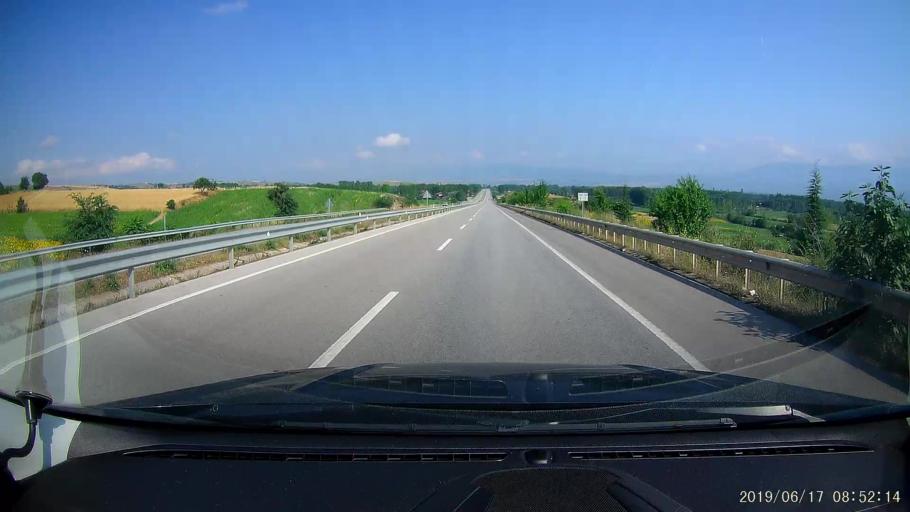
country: TR
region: Tokat
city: Erbaa
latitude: 40.6949
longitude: 36.5001
